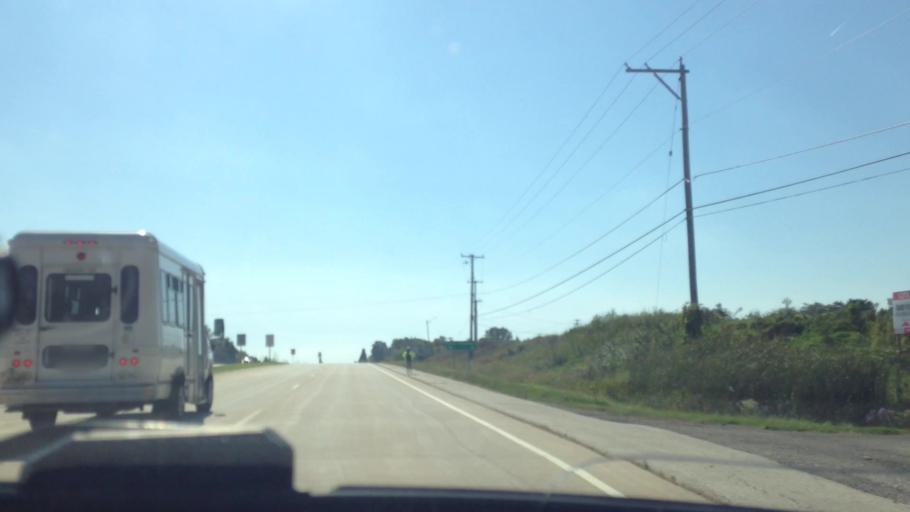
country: US
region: Wisconsin
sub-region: Ozaukee County
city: Saukville
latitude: 43.3548
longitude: -87.9125
